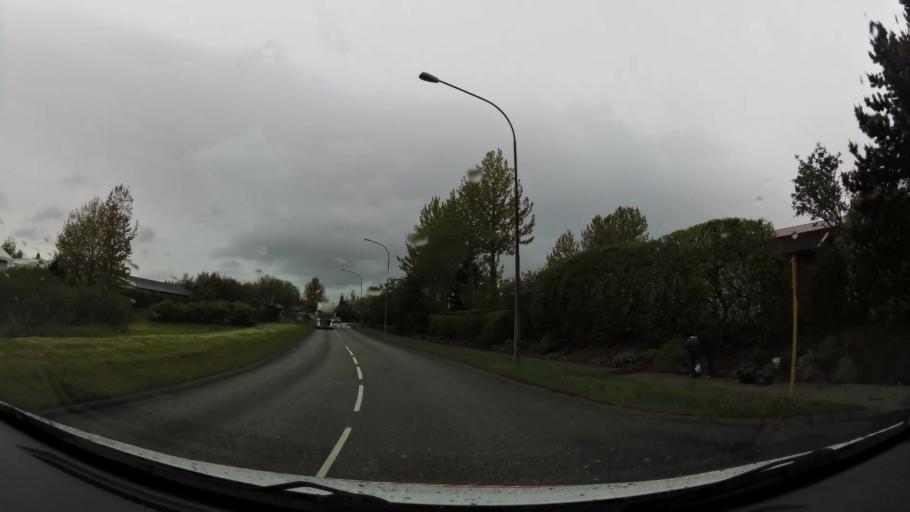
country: IS
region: Capital Region
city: Hafnarfjoerdur
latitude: 64.0675
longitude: -21.9349
